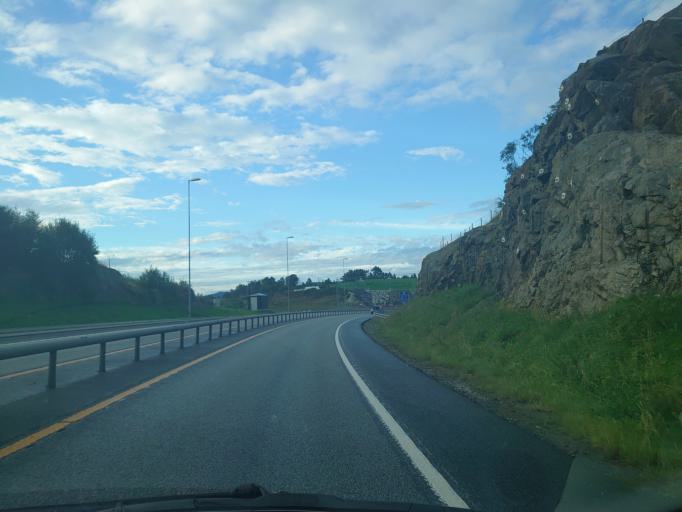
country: NO
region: Hordaland
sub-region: Lindas
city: Isdalsto
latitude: 60.5371
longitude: 5.2586
